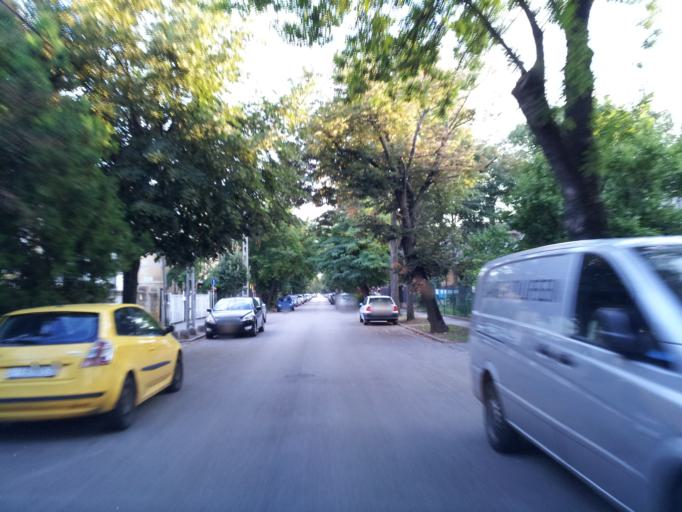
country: HU
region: Budapest
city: Budapest XIV. keruelet
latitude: 47.5253
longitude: 19.1126
